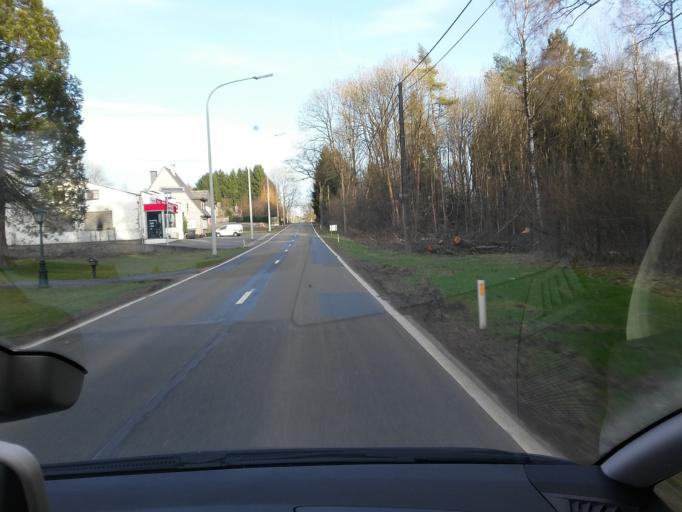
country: BE
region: Wallonia
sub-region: Province du Luxembourg
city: Libin
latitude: 50.0111
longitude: 5.2010
